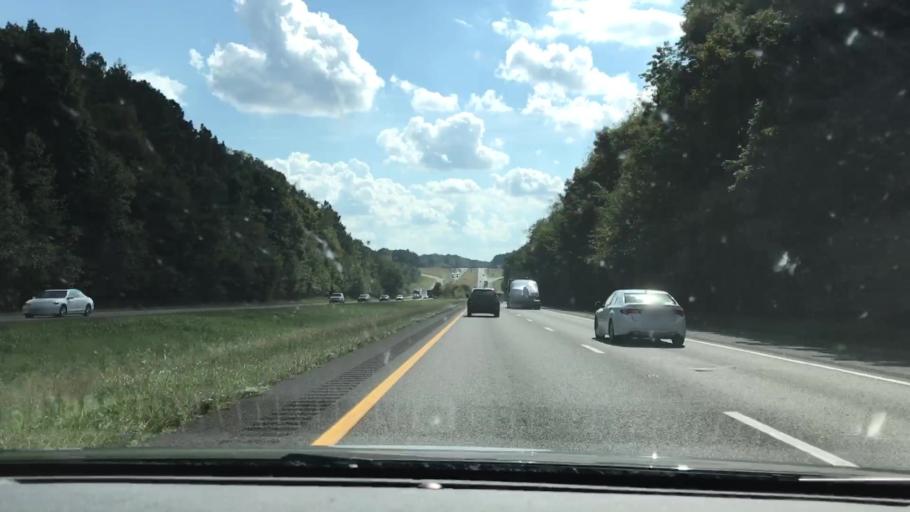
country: US
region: Tennessee
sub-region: Robertson County
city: Cross Plains
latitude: 36.5373
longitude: -86.6393
